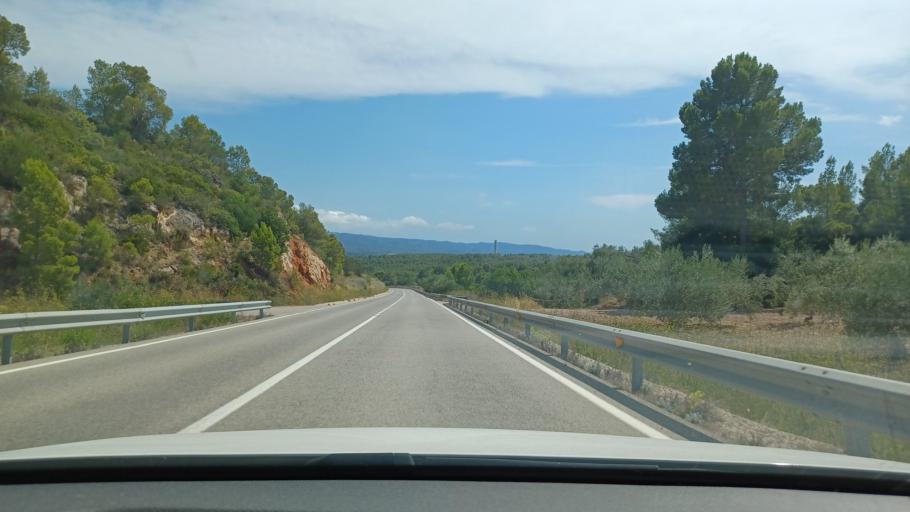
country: ES
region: Catalonia
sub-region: Provincia de Tarragona
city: Tivenys
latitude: 40.9400
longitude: 0.4658
